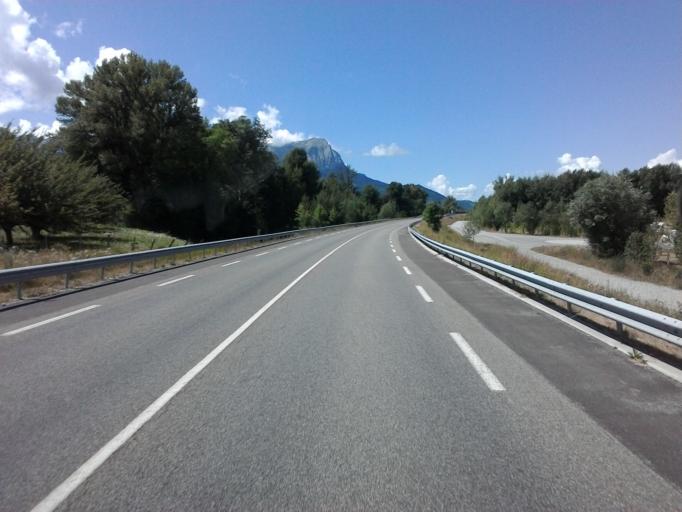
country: FR
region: Provence-Alpes-Cote d'Azur
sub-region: Departement des Hautes-Alpes
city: Embrun
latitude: 44.5543
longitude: 6.5016
